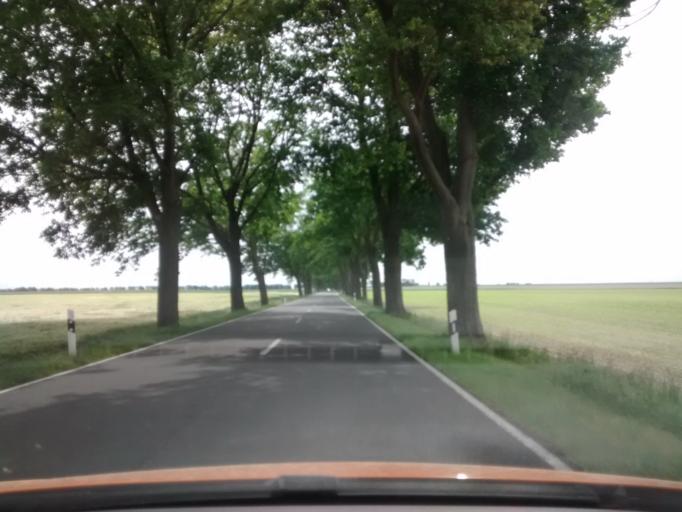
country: DE
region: Brandenburg
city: Juterbog
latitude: 51.9196
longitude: 13.1288
